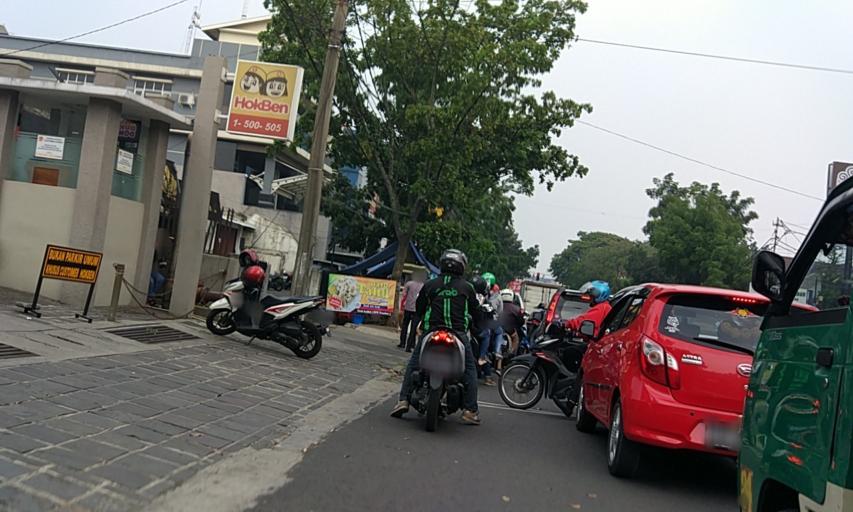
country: ID
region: West Java
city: Bandung
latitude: -6.9028
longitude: 107.5976
